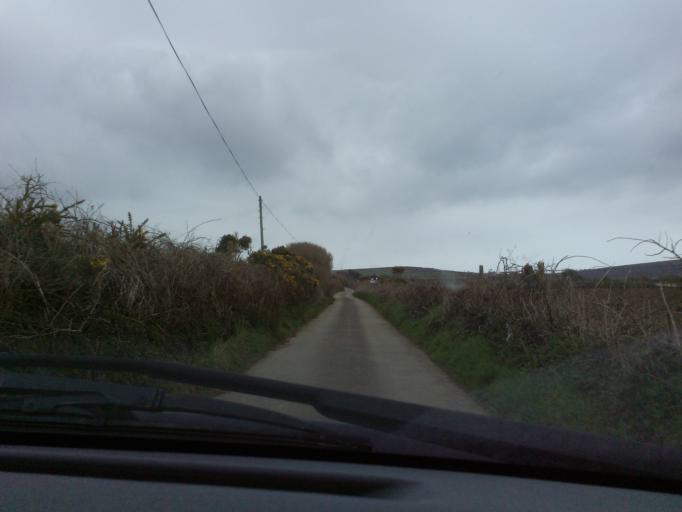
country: GB
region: England
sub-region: Cornwall
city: Saint Just
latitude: 50.1069
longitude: -5.6688
